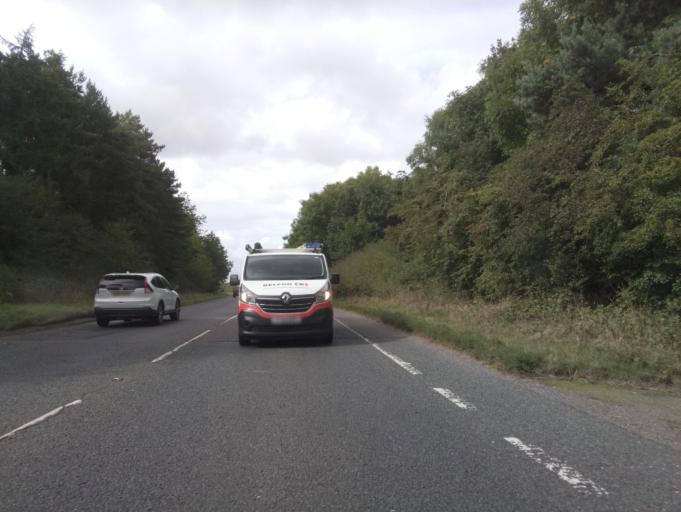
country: GB
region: England
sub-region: Telford and Wrekin
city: Newport
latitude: 52.7787
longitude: -2.3665
